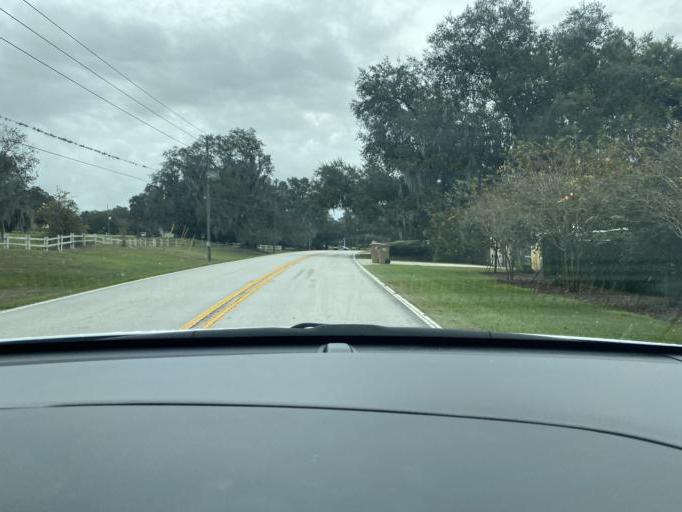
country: US
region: Florida
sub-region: Lake County
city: Minneola
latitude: 28.5894
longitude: -81.7719
